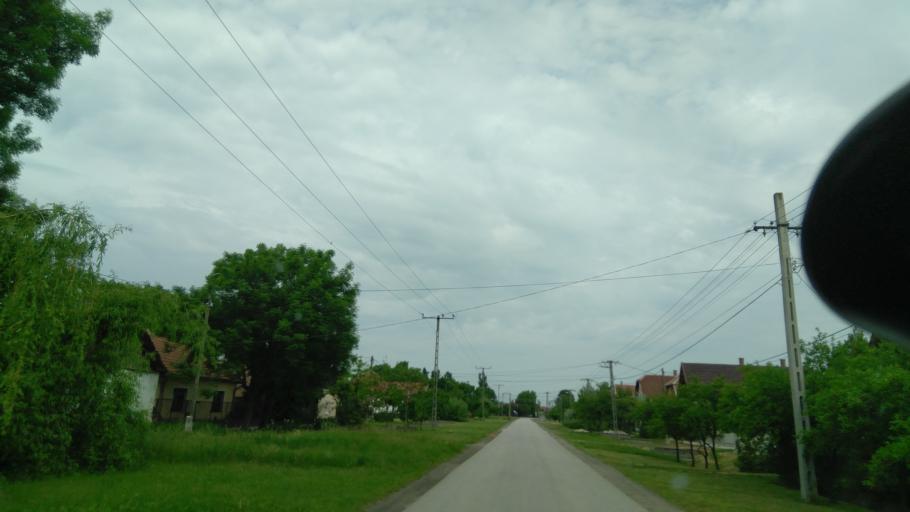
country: HU
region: Bekes
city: Szeghalom
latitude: 47.0245
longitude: 21.1679
